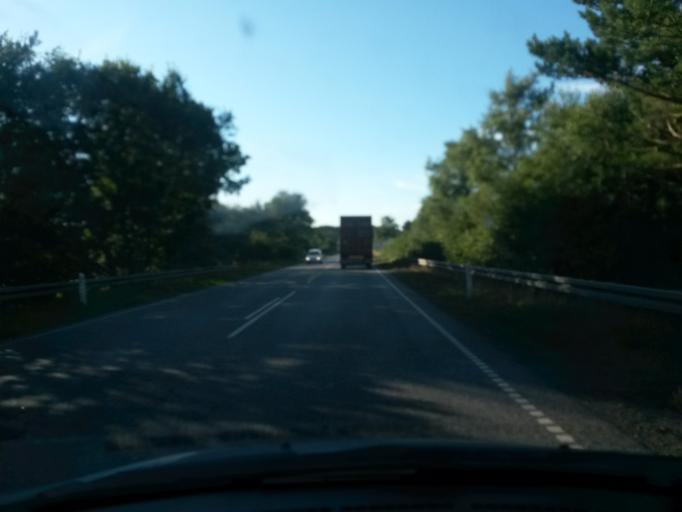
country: DK
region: Central Jutland
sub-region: Viborg Kommune
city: Bjerringbro
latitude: 56.3113
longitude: 9.5914
